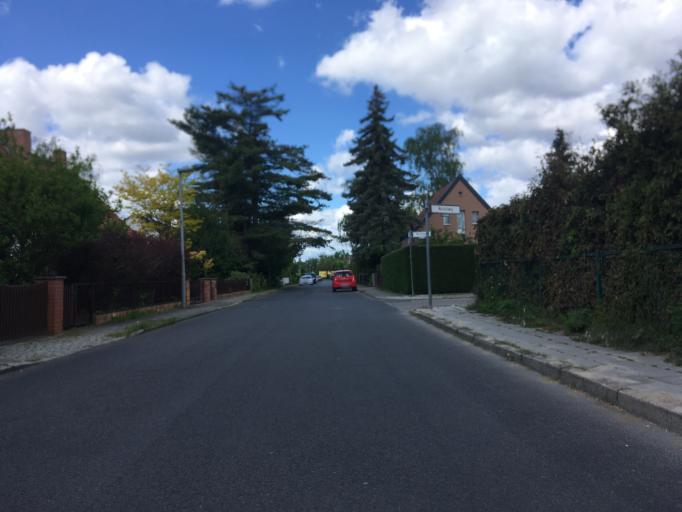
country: DE
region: Berlin
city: Altglienicke
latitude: 52.4093
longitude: 13.5302
